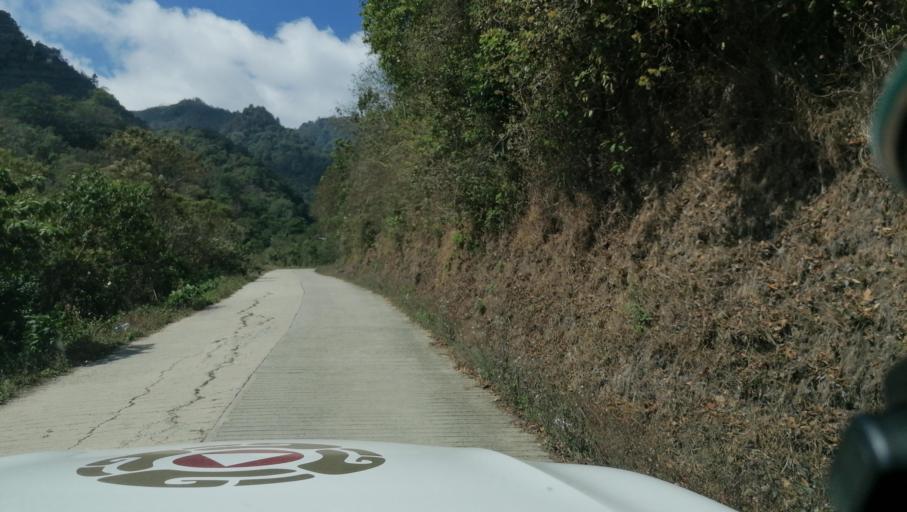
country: GT
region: San Marcos
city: Tacana
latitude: 15.2029
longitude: -92.1977
